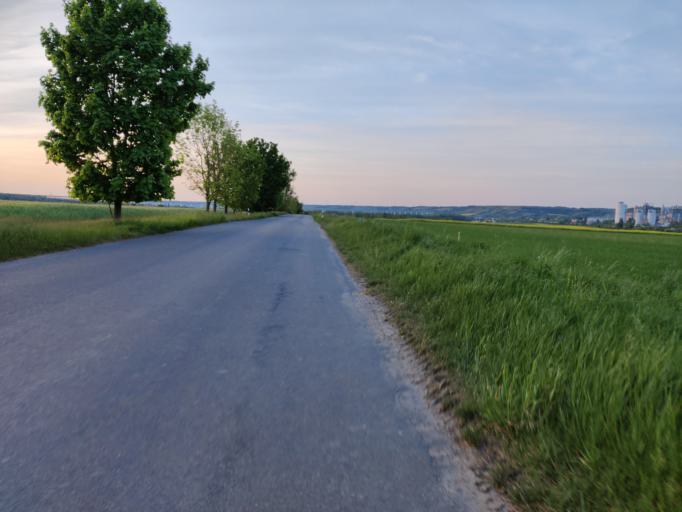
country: DE
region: Saxony-Anhalt
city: Karsdorf
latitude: 51.2535
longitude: 11.6444
